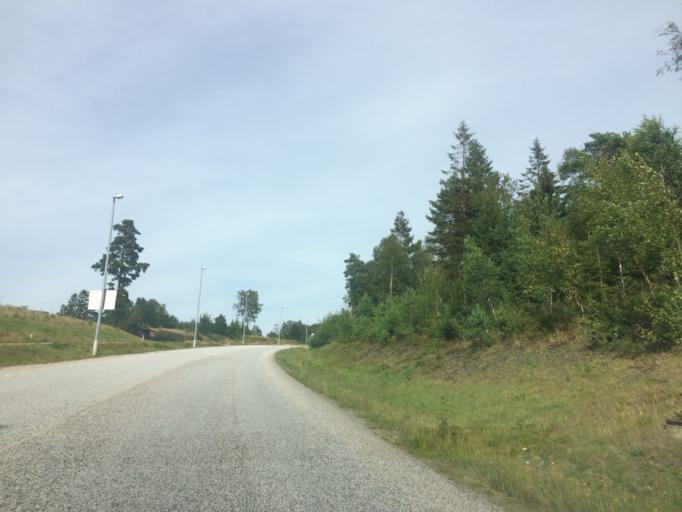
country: SE
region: Vaestra Goetaland
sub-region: Partille Kommun
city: Ojersjo
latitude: 57.6819
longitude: 12.0962
